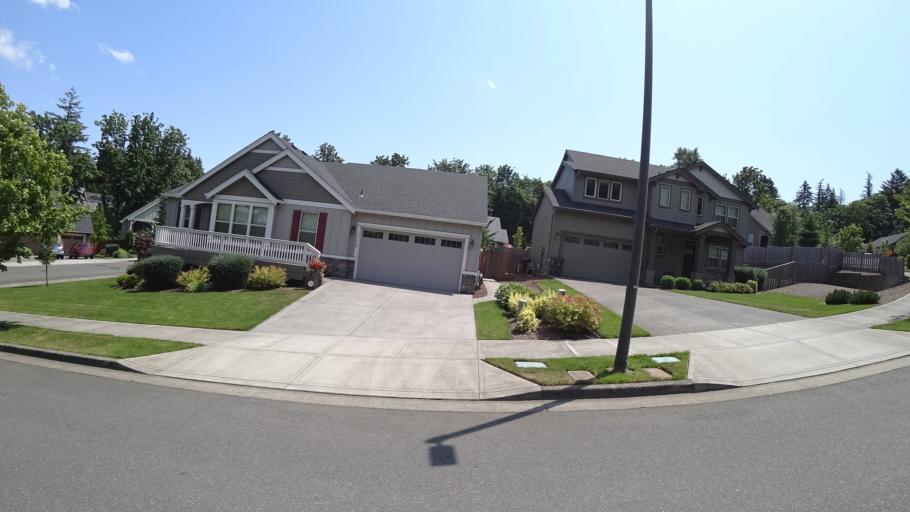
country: US
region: Oregon
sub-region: Clackamas County
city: Happy Valley
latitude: 45.4549
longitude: -122.5428
